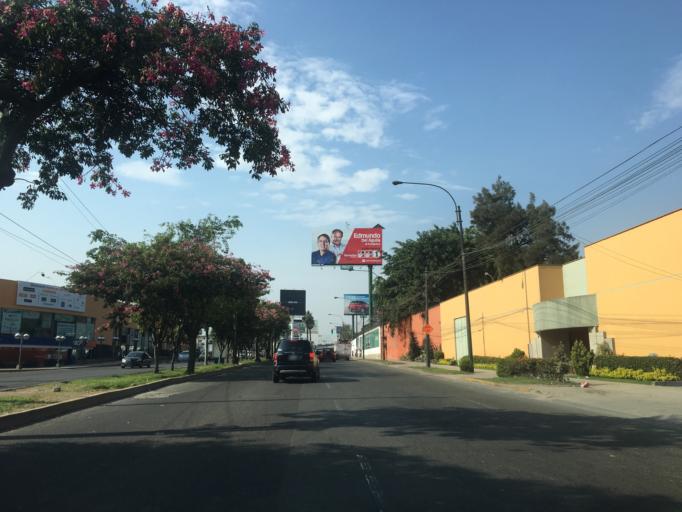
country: PE
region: Lima
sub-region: Lima
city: La Molina
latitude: -12.0808
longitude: -76.9667
